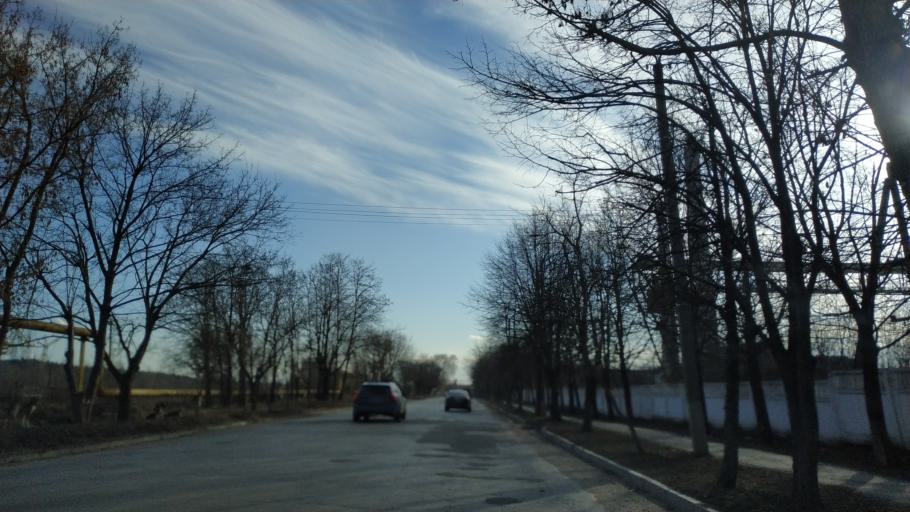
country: MD
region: Chisinau
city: Chisinau
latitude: 47.0340
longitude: 28.8973
